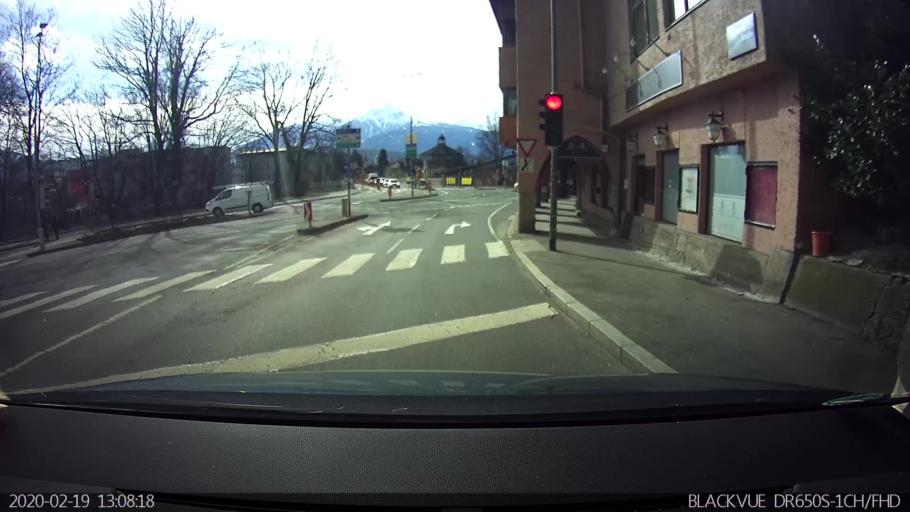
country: AT
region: Tyrol
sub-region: Innsbruck Stadt
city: Innsbruck
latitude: 47.2815
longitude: 11.4059
